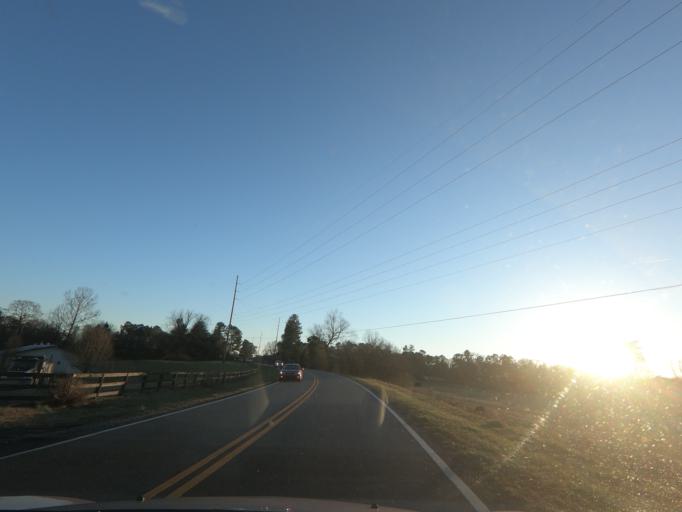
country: US
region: Georgia
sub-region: Forsyth County
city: Cumming
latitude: 34.3077
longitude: -84.1496
